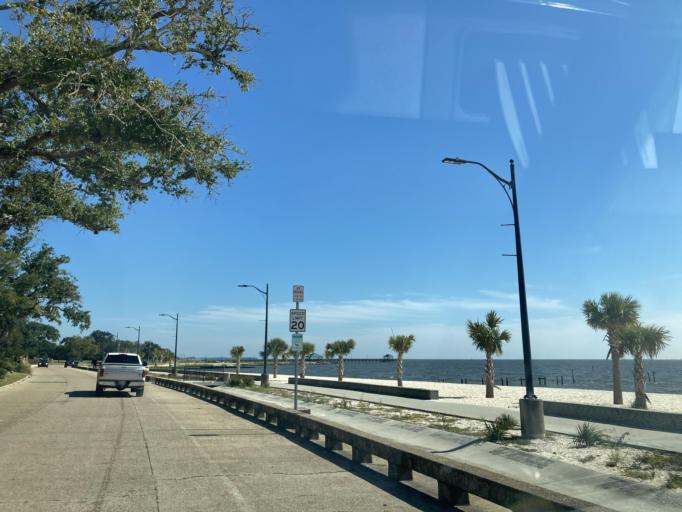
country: US
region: Mississippi
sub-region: Jackson County
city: Ocean Springs
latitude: 30.4073
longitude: -88.8333
